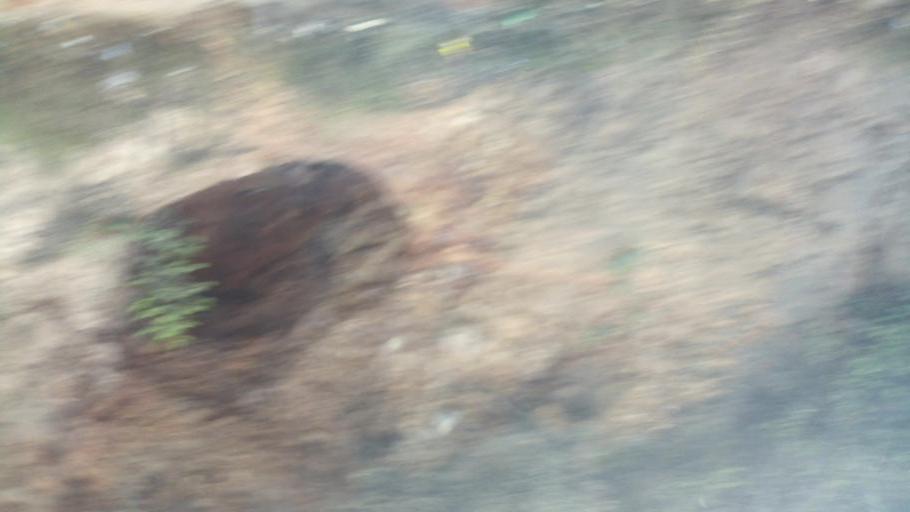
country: KE
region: Kiambu
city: Limuru
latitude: -1.0659
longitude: 36.6019
